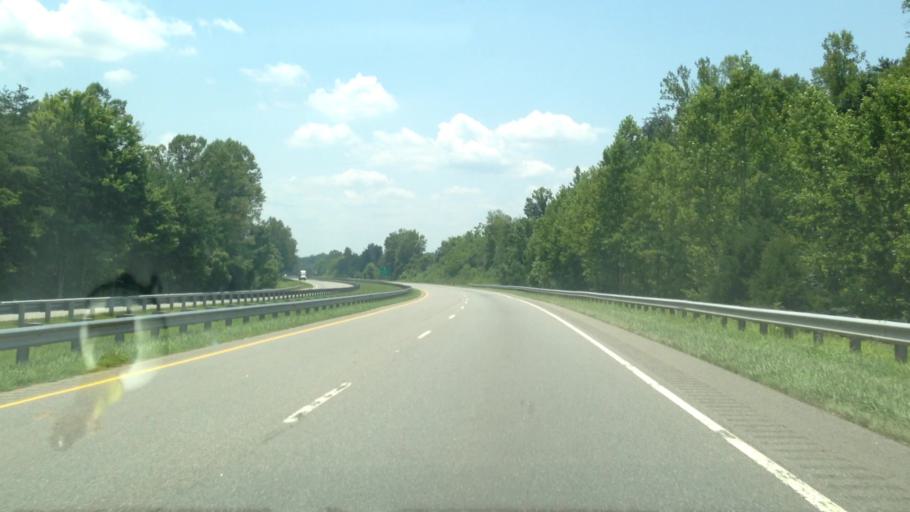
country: US
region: North Carolina
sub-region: Rockingham County
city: Stoneville
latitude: 36.4901
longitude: -79.9254
